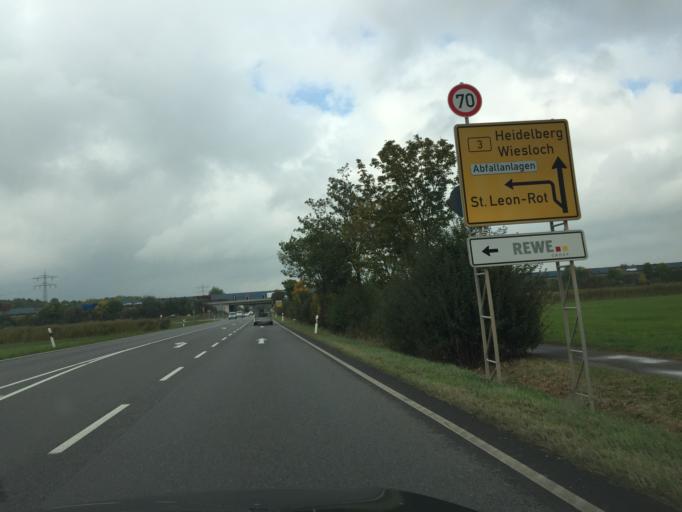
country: DE
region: Baden-Wuerttemberg
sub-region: Karlsruhe Region
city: Malsch
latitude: 49.2693
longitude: 8.6673
